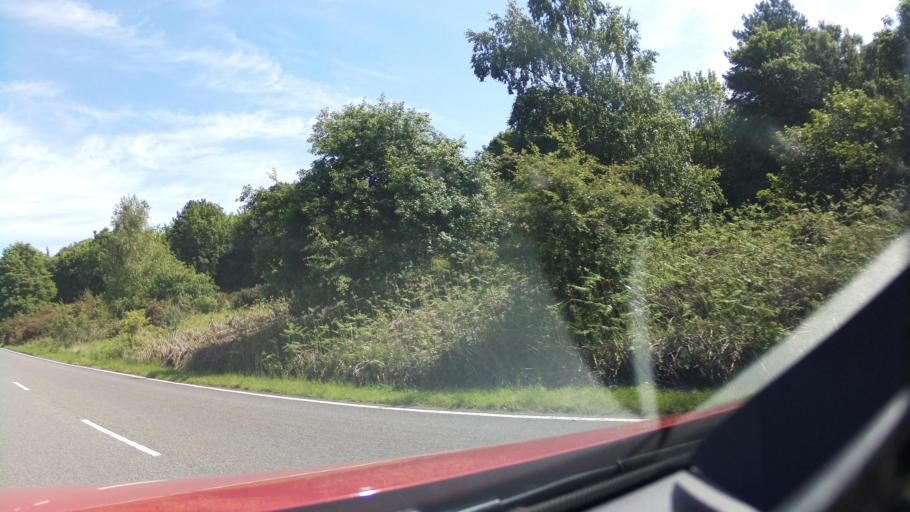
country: GB
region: England
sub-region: North Lincolnshire
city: Manton
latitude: 53.5251
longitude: -0.5793
